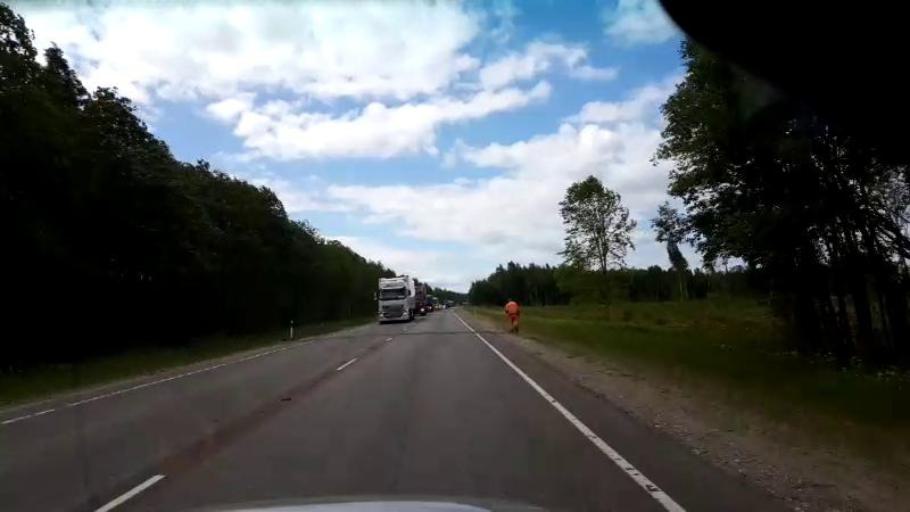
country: LV
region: Salacgrivas
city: Ainazi
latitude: 58.0140
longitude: 24.4937
